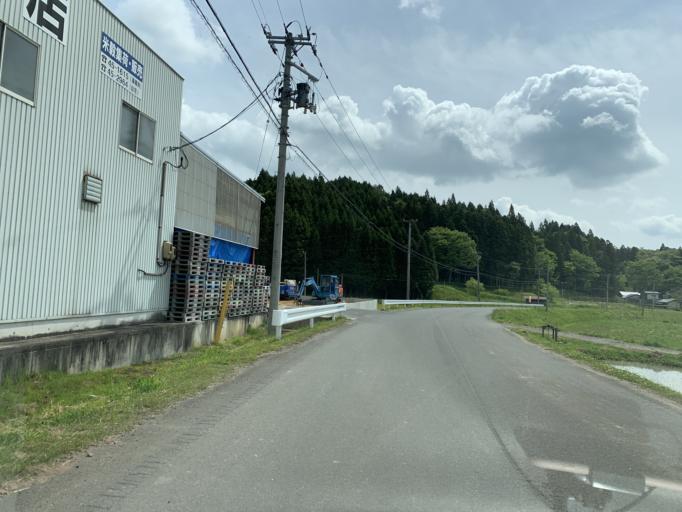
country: JP
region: Iwate
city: Ichinoseki
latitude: 38.8590
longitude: 141.0007
